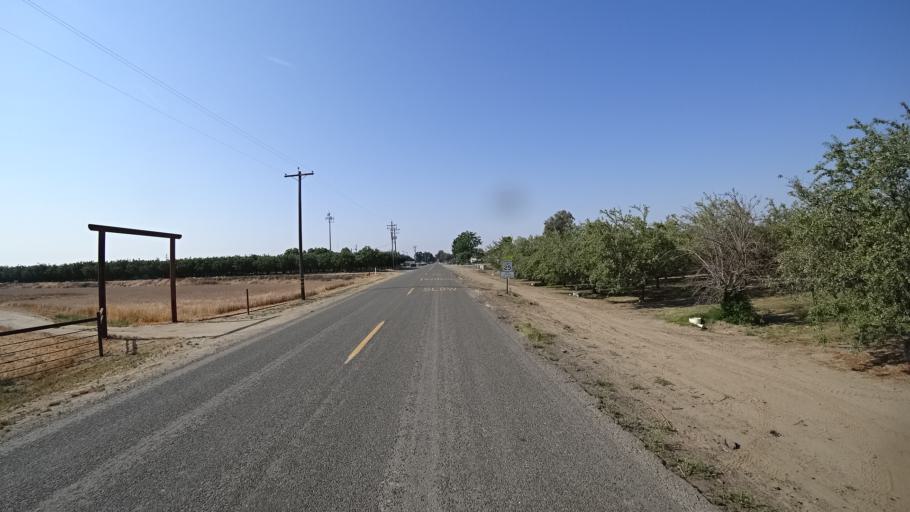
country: US
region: California
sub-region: Fresno County
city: Riverdale
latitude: 36.3639
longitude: -119.8342
